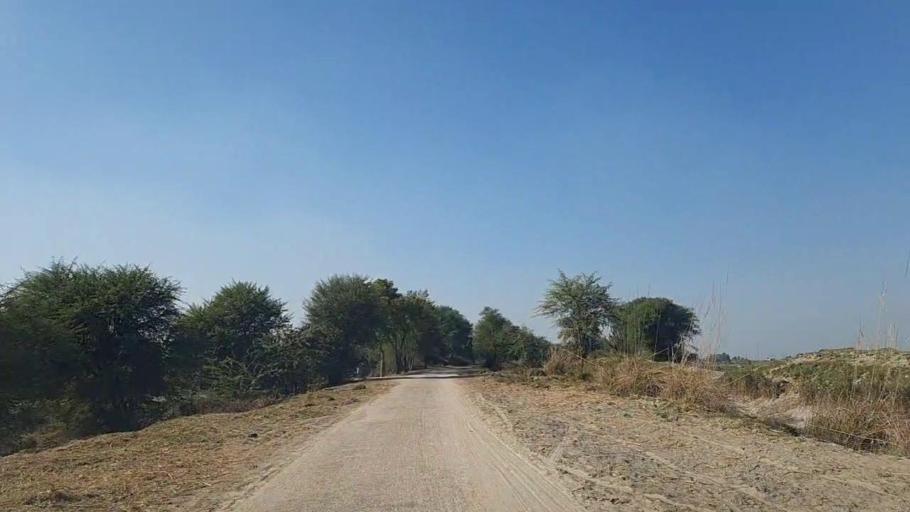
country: PK
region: Sindh
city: Shahpur Chakar
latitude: 26.2147
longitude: 68.6081
